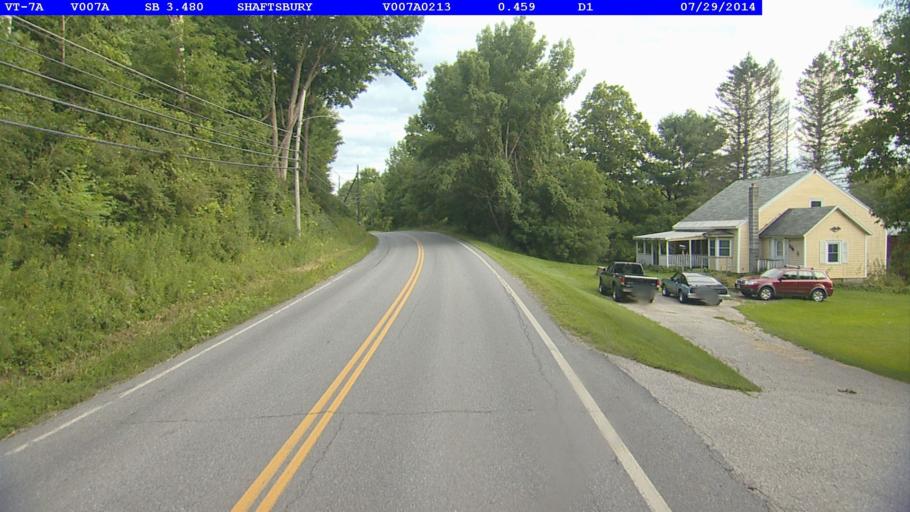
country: US
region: Vermont
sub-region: Bennington County
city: North Bennington
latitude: 42.9393
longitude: -73.2102
